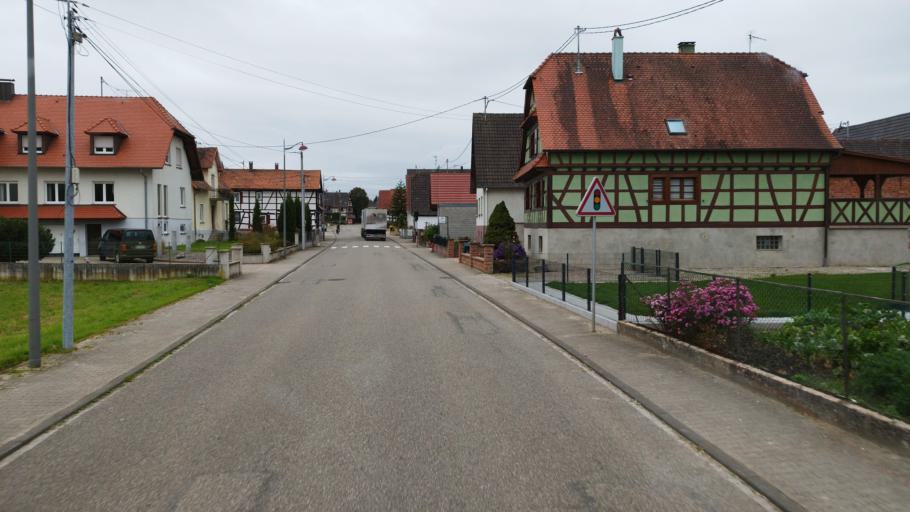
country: DE
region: Rheinland-Pfalz
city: Scheibenhardt
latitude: 48.9733
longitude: 8.1099
